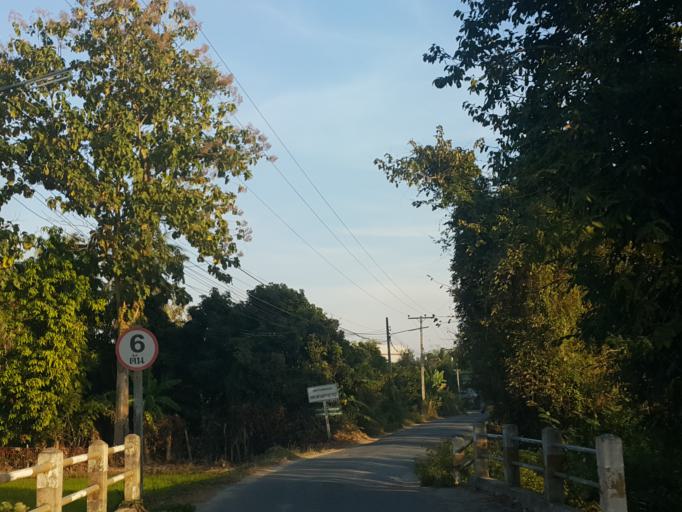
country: TH
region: Chiang Mai
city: San Sai
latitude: 18.8221
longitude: 99.0899
